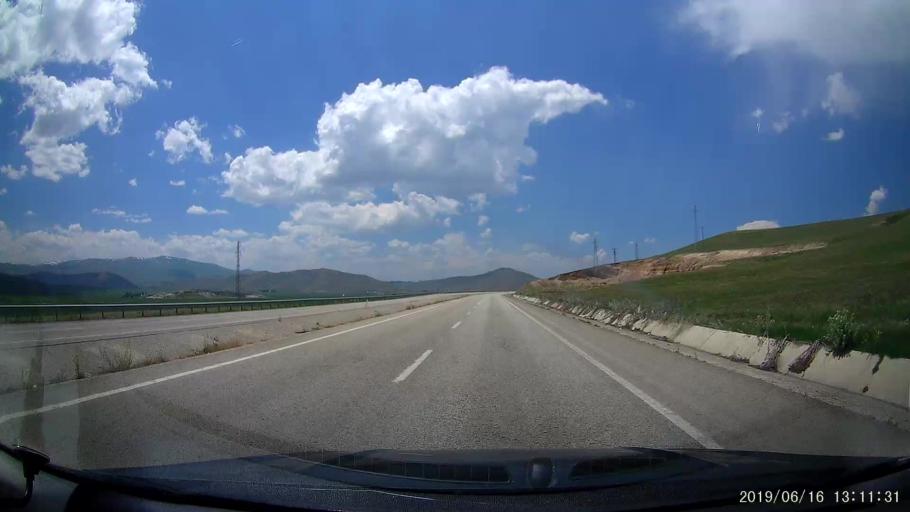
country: TR
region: Agri
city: Diyadin
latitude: 39.5919
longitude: 43.6057
